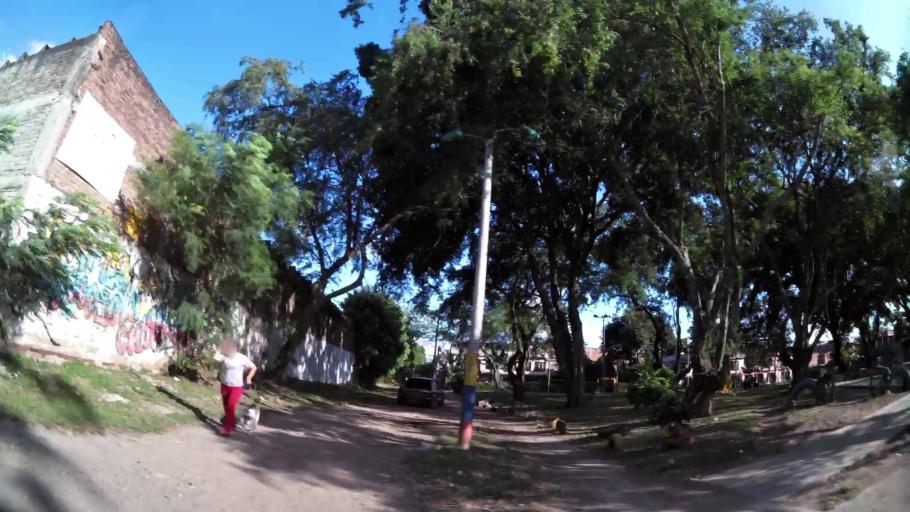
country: CO
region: Valle del Cauca
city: Cali
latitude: 3.4051
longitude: -76.5032
